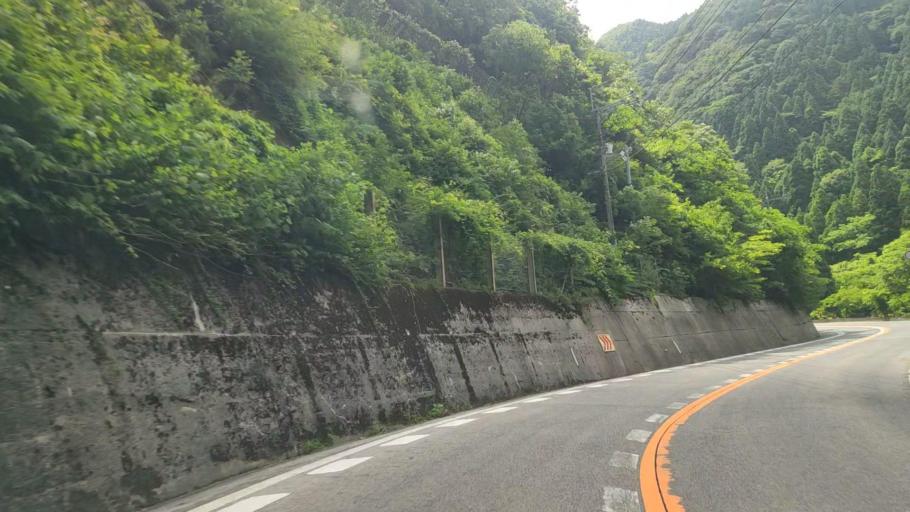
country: JP
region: Okayama
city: Niimi
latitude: 35.2104
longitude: 133.4707
